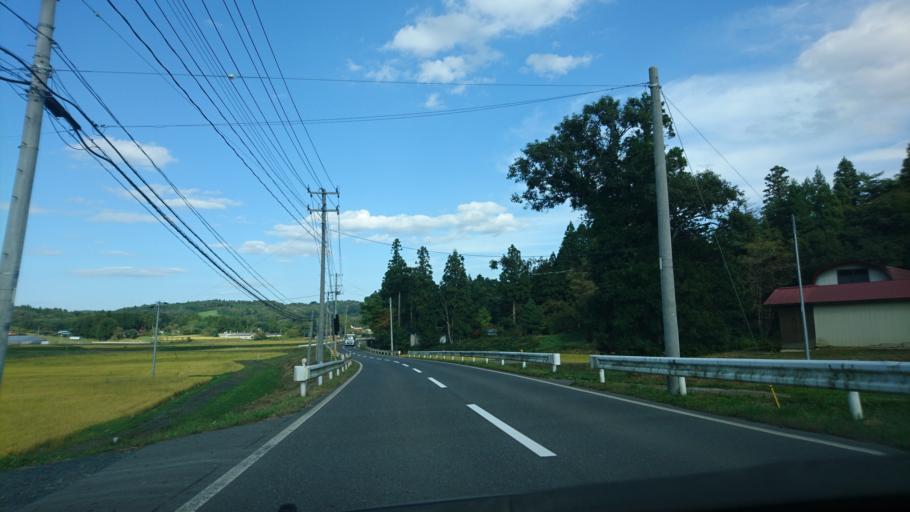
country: JP
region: Iwate
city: Ichinoseki
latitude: 38.8334
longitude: 141.2280
